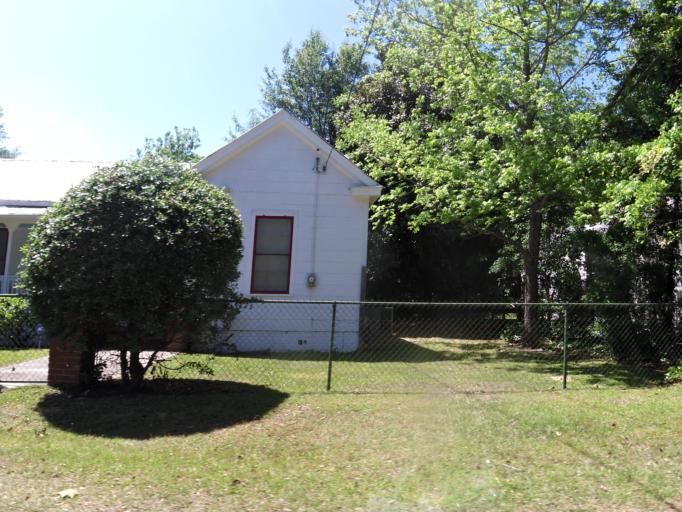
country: US
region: South Carolina
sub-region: Aiken County
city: Aiken
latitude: 33.5587
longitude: -81.7108
